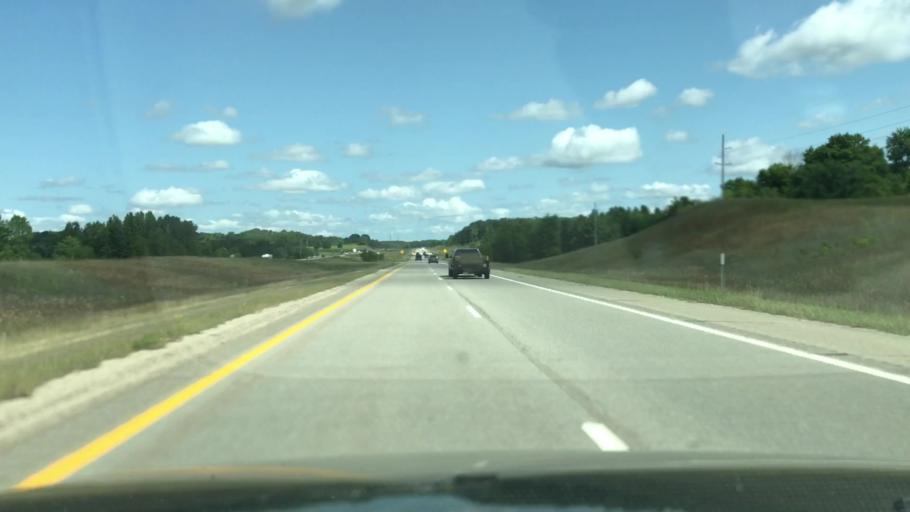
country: US
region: Michigan
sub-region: Mecosta County
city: Big Rapids
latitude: 43.7807
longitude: -85.5338
